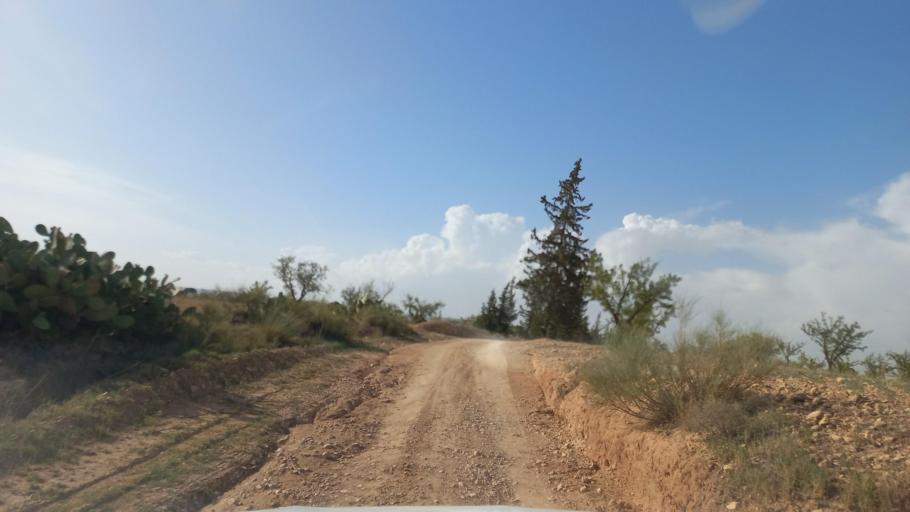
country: TN
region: Al Qasrayn
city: Kasserine
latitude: 35.2290
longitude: 8.9674
